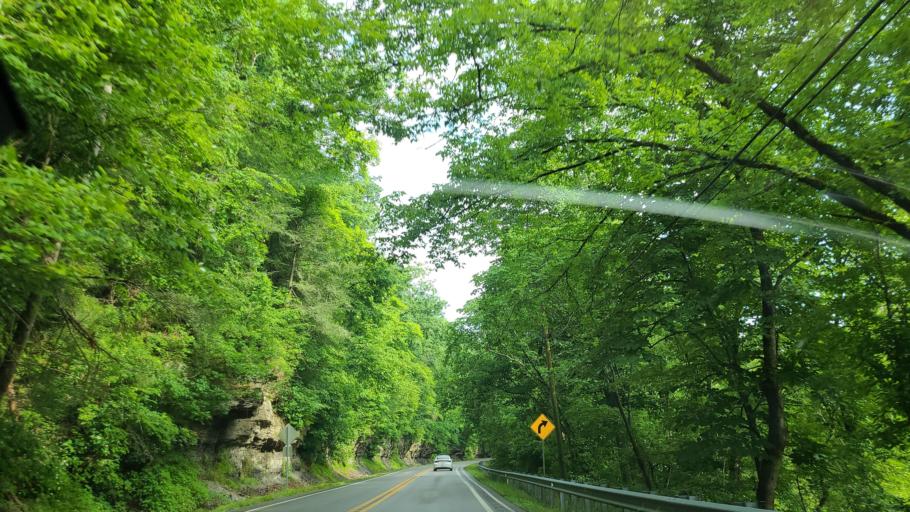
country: US
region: Kentucky
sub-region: Whitley County
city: Williamsburg
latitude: 36.7336
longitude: -84.1048
